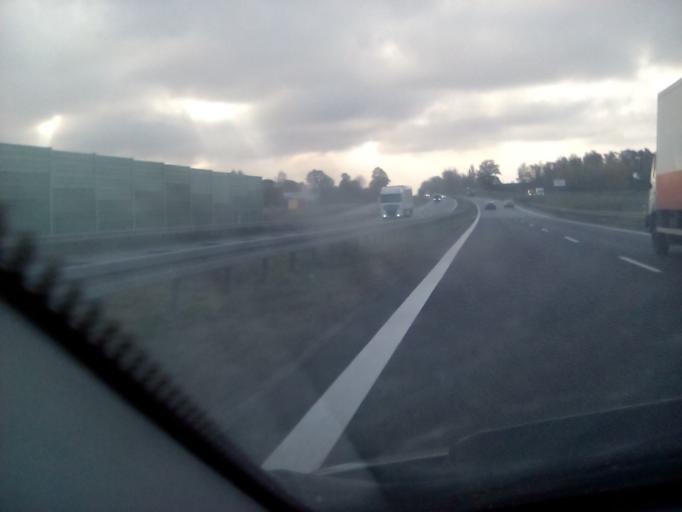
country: PL
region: Masovian Voivodeship
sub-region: Powiat bialobrzeski
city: Promna
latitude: 51.6882
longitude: 20.9348
